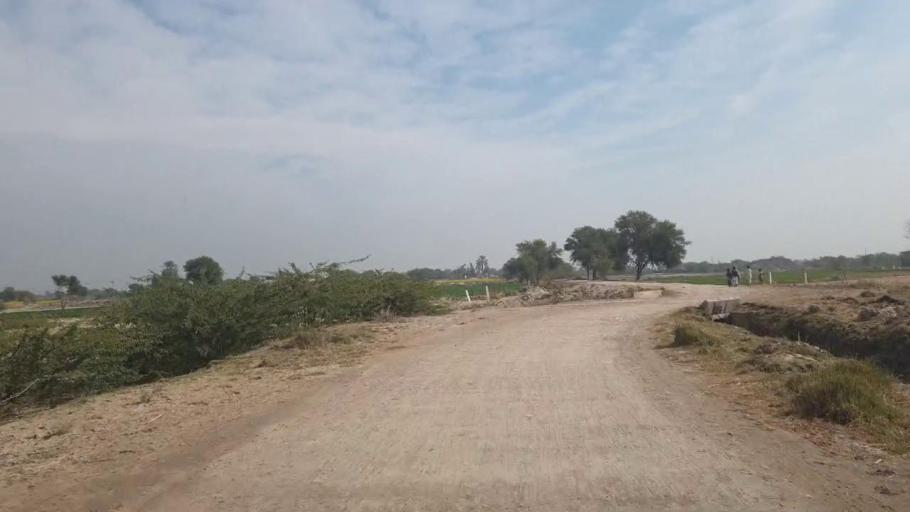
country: PK
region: Sindh
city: Nawabshah
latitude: 26.1140
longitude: 68.4903
